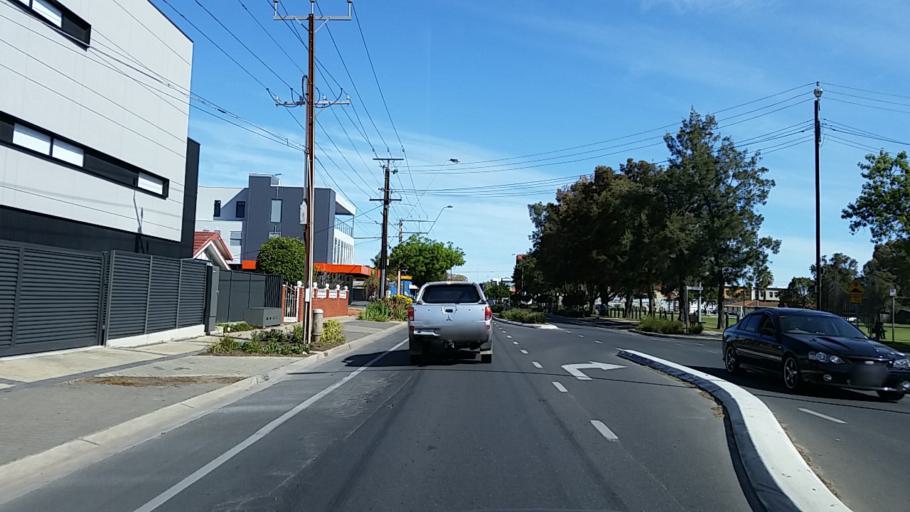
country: AU
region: South Australia
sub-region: Prospect
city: Prospect
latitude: -34.8878
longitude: 138.5850
